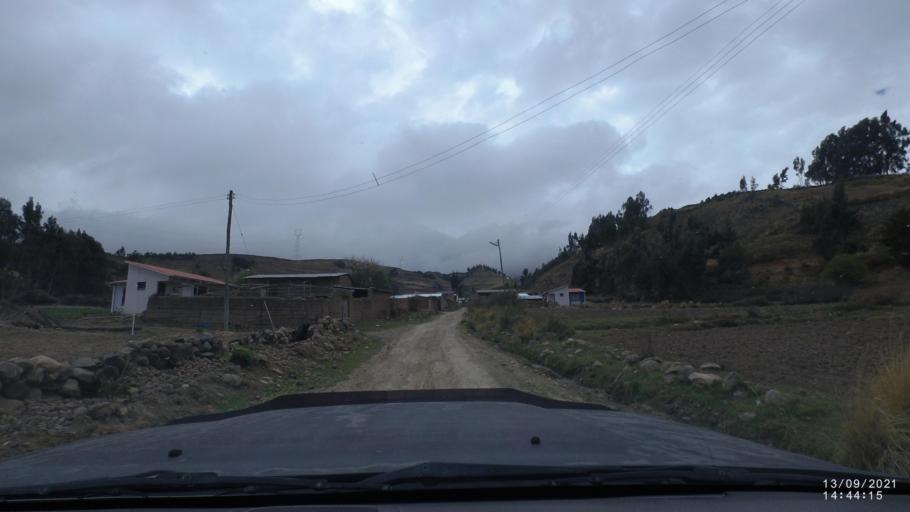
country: BO
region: Cochabamba
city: Colomi
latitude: -17.3594
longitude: -65.8115
